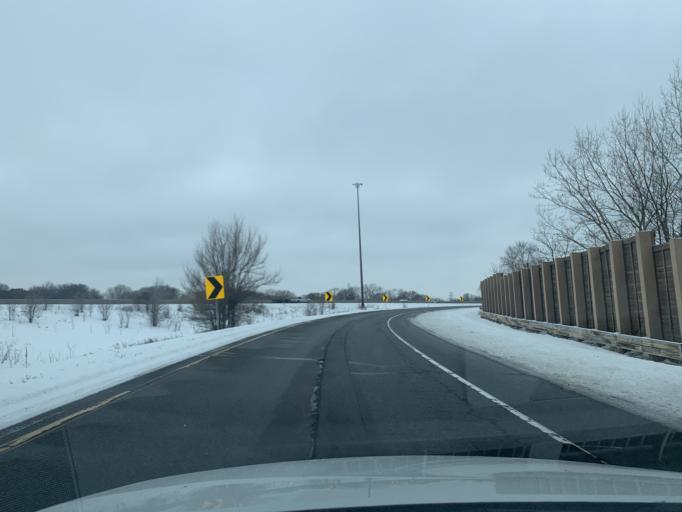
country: US
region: Minnesota
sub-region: Anoka County
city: Coon Rapids
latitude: 45.1438
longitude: -93.2716
